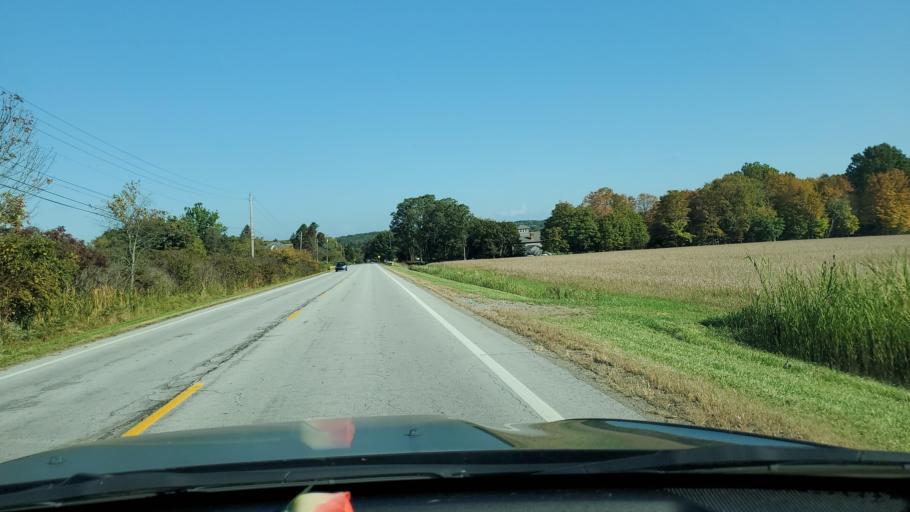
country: US
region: Ohio
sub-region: Trumbull County
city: Brookfield Center
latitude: 41.2597
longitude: -80.5683
